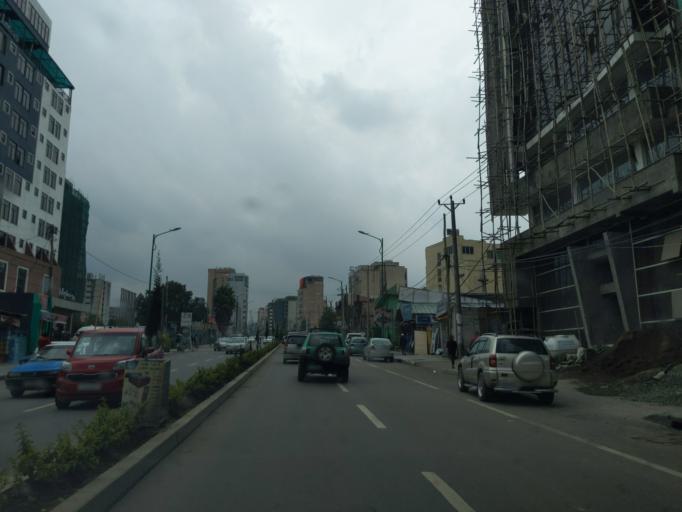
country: ET
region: Adis Abeba
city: Addis Ababa
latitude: 8.9902
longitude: 38.7658
